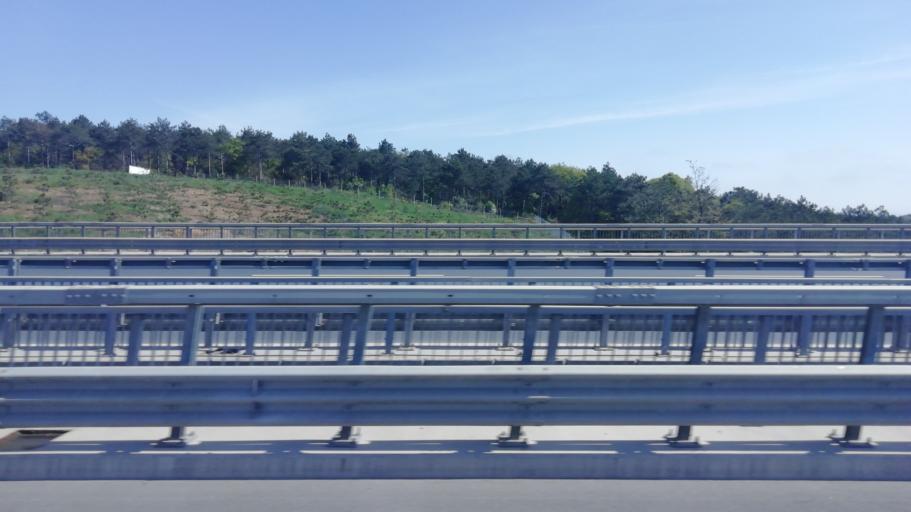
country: TR
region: Istanbul
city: Arikoey
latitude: 41.2245
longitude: 29.0754
